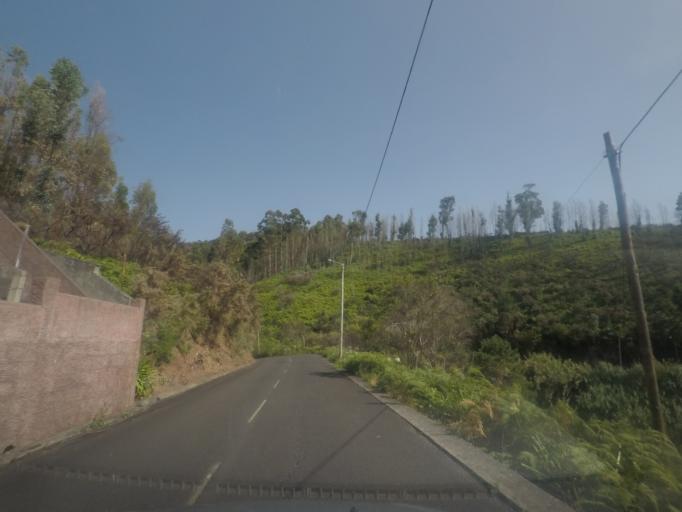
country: PT
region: Madeira
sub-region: Calheta
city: Faja da Ovelha
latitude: 32.8285
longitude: -17.2314
